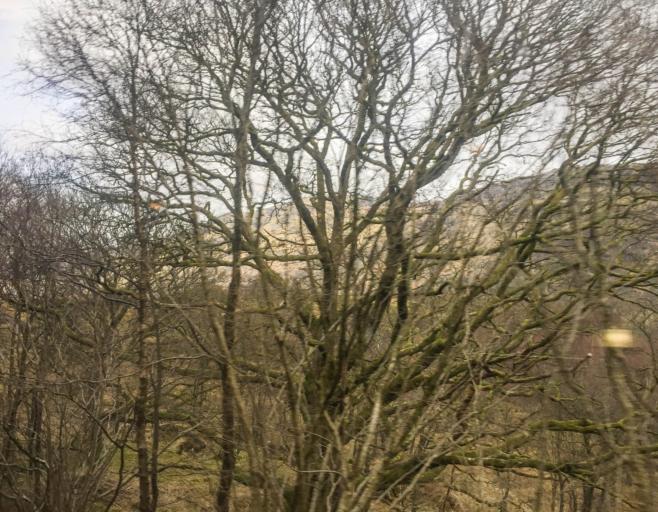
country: GB
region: Scotland
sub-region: Argyll and Bute
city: Garelochhead
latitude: 56.2658
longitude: -4.7057
